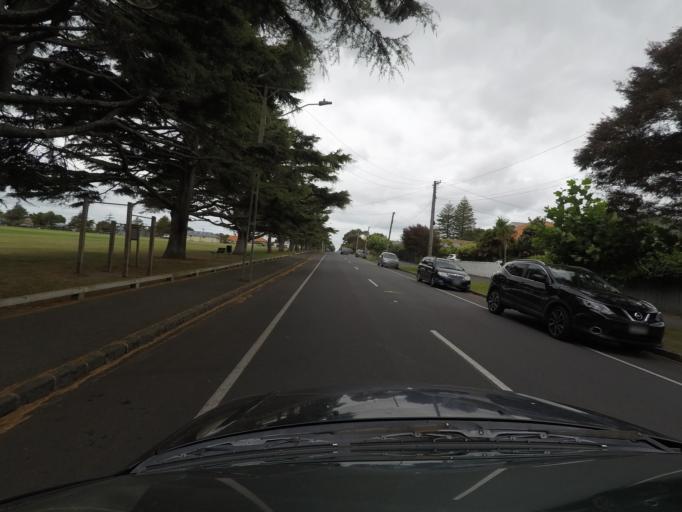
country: NZ
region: Auckland
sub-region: Auckland
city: Rosebank
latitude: -36.8662
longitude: 174.7032
